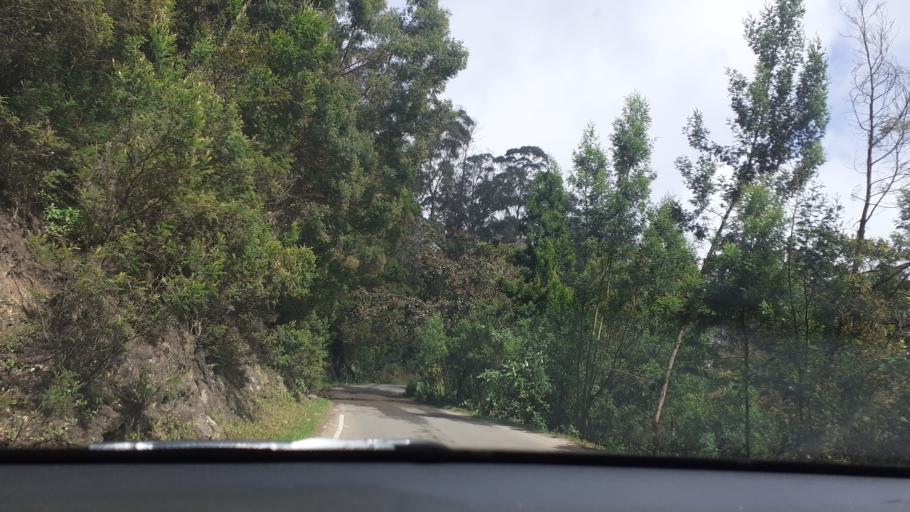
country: IN
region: Tamil Nadu
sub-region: Dindigul
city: Kodaikanal
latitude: 10.2339
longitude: 77.4247
